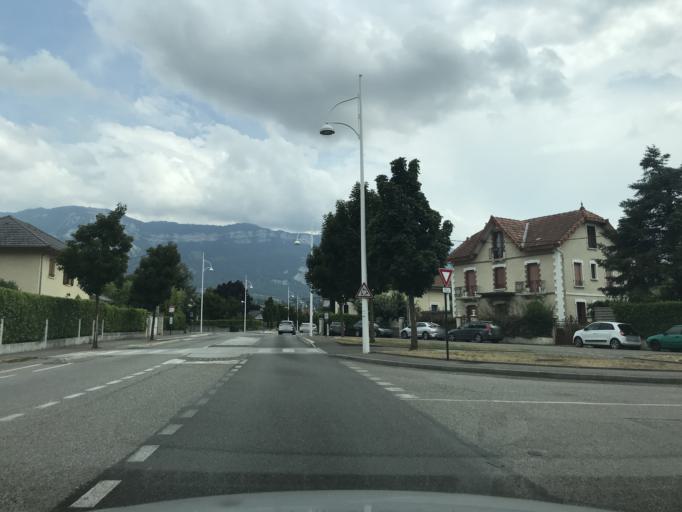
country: FR
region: Rhone-Alpes
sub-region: Departement de la Savoie
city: Tresserve
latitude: 45.6985
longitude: 5.8929
